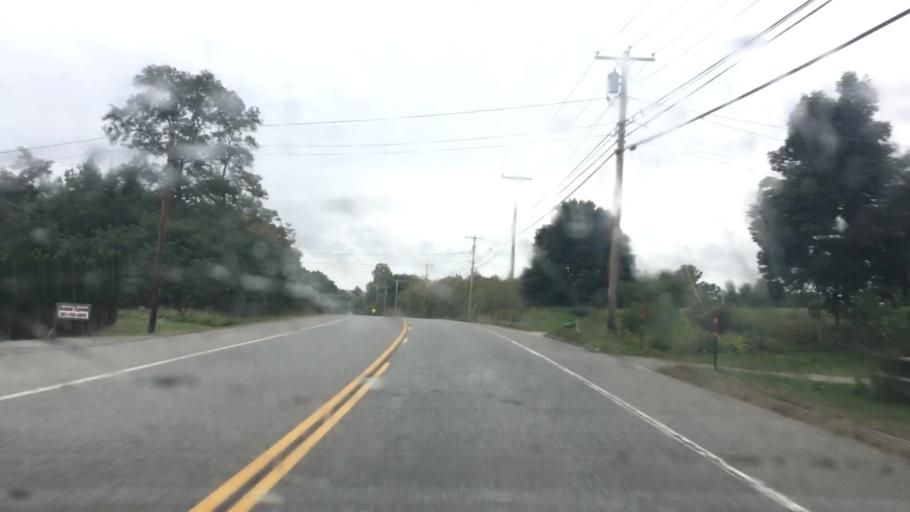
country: US
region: Maine
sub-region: Penobscot County
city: Orrington
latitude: 44.7149
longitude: -68.8272
